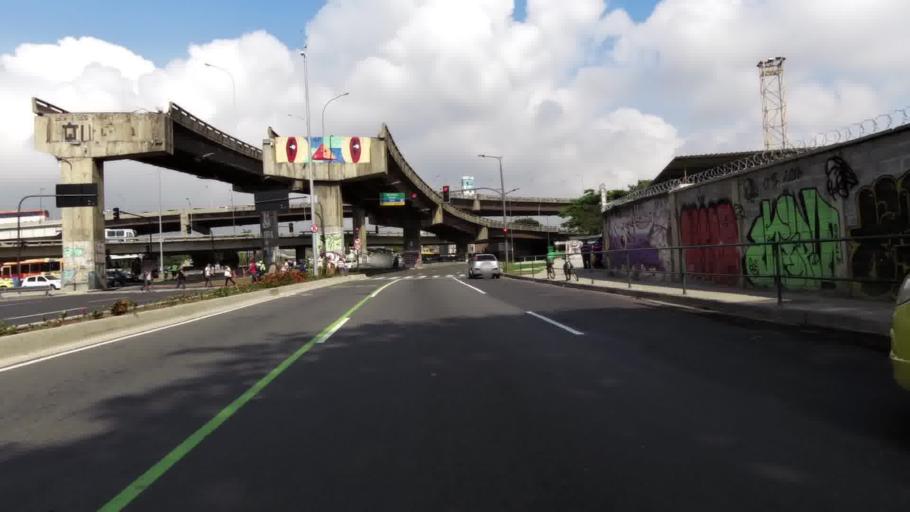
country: BR
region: Rio de Janeiro
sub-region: Rio De Janeiro
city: Rio de Janeiro
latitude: -22.8983
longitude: -43.2095
